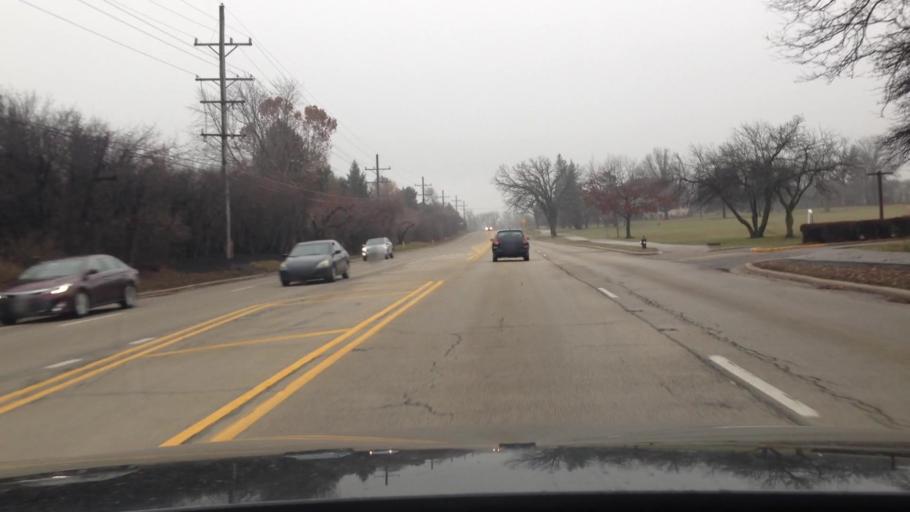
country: US
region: Illinois
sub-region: DuPage County
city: Oakbrook Terrace
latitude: 41.8306
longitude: -87.9719
